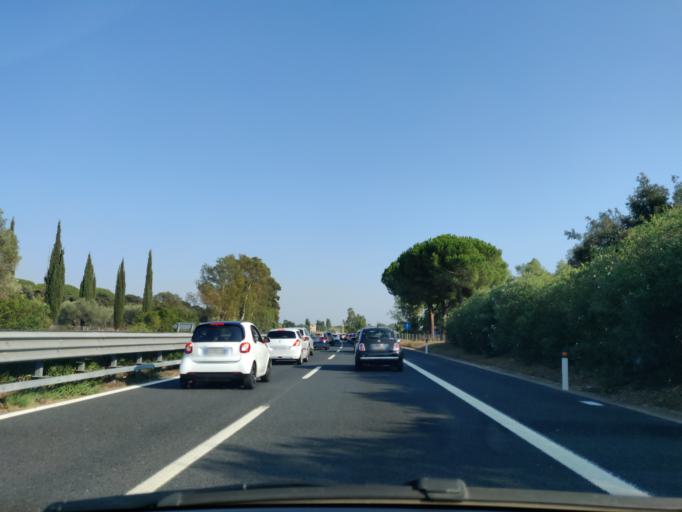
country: IT
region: Latium
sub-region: Citta metropolitana di Roma Capitale
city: Valcanneto
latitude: 41.9391
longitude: 12.1486
